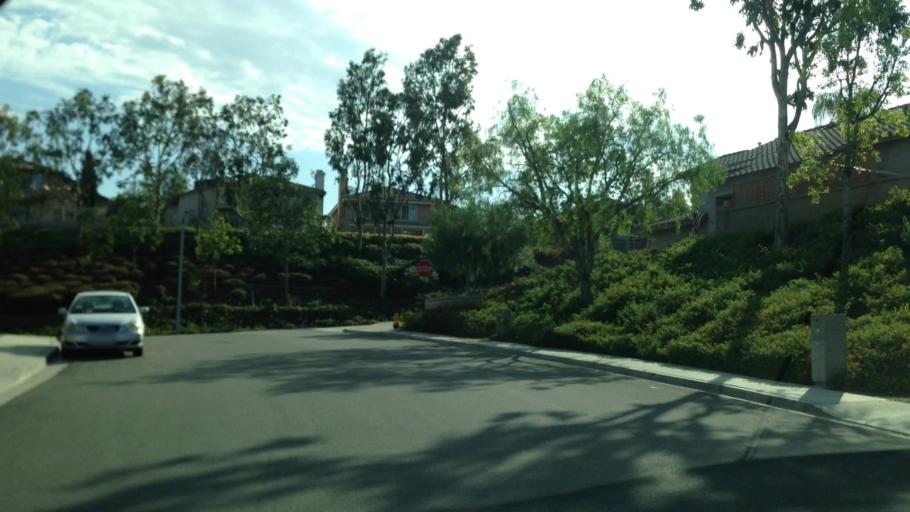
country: US
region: California
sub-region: Orange County
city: Rancho Santa Margarita
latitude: 33.6452
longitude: -117.6214
